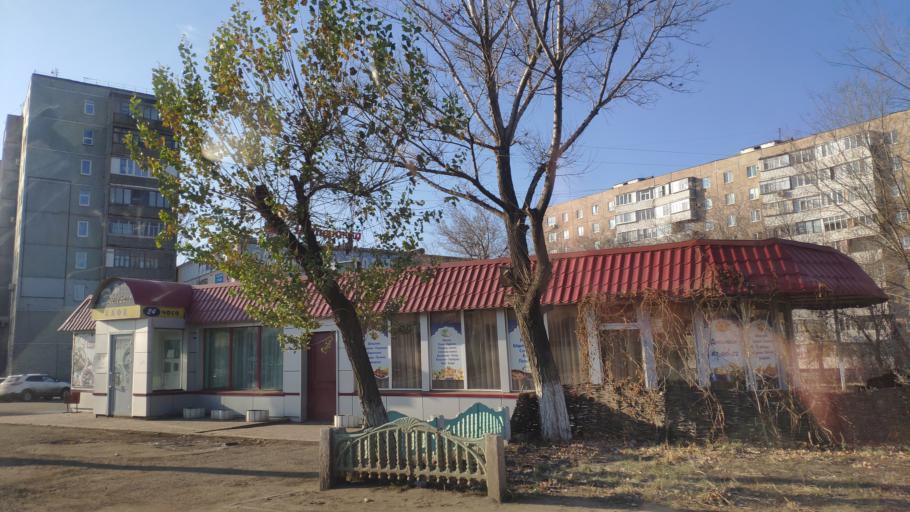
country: RU
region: Orenburg
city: Prigorodnyy
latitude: 51.7790
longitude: 55.1898
